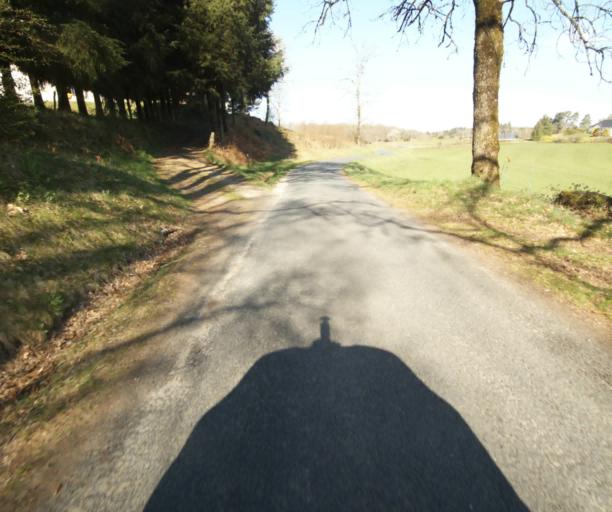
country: FR
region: Limousin
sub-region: Departement de la Correze
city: Correze
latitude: 45.2745
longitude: 1.8860
